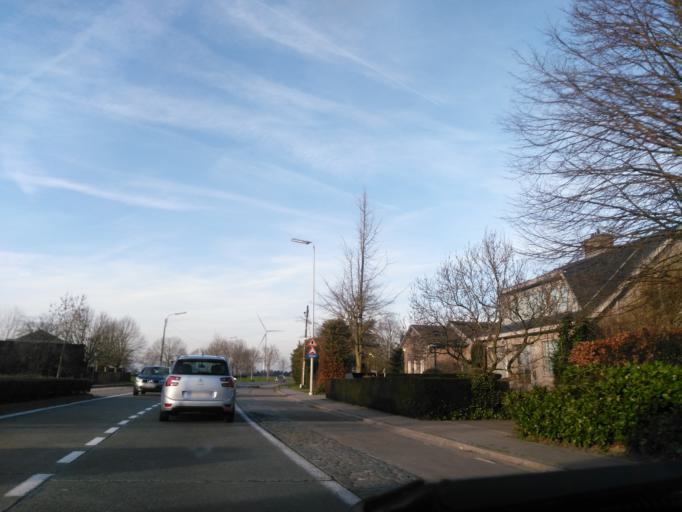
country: BE
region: Flanders
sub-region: Provincie Oost-Vlaanderen
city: Beveren
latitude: 51.2256
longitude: 4.1914
